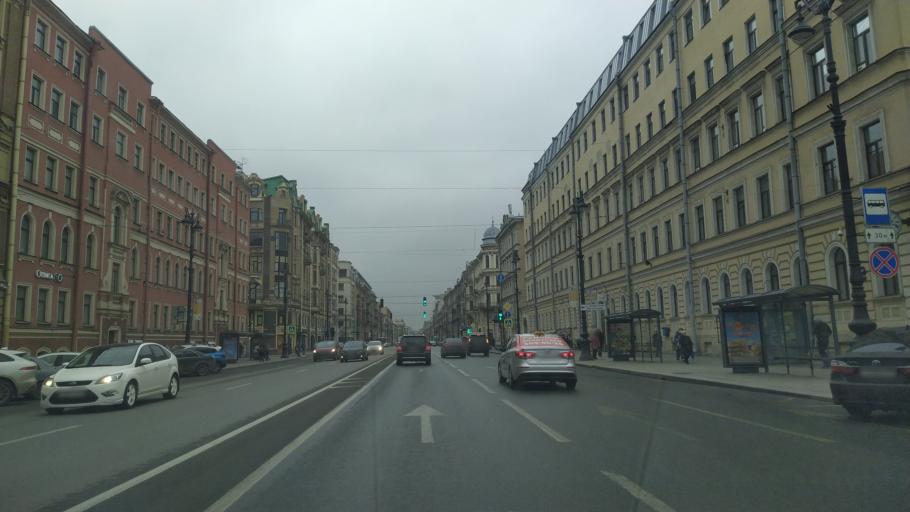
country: RU
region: St.-Petersburg
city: Centralniy
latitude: 59.9254
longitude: 30.3805
